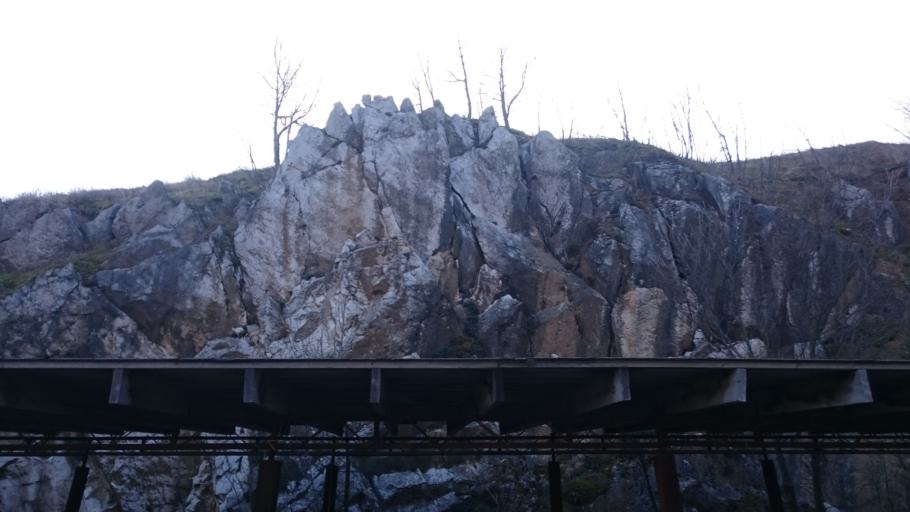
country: HU
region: Baranya
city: Villany
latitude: 45.8559
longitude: 18.4301
